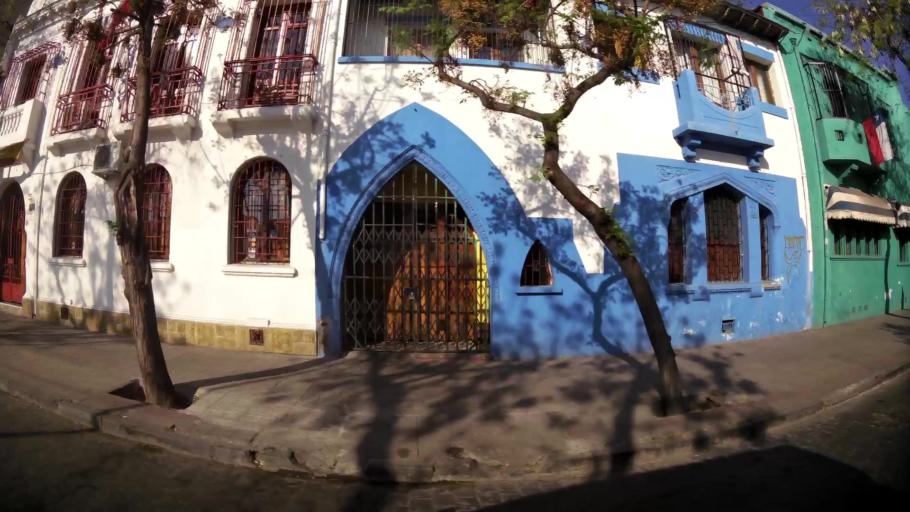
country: CL
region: Santiago Metropolitan
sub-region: Provincia de Santiago
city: Santiago
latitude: -33.4445
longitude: -70.6696
